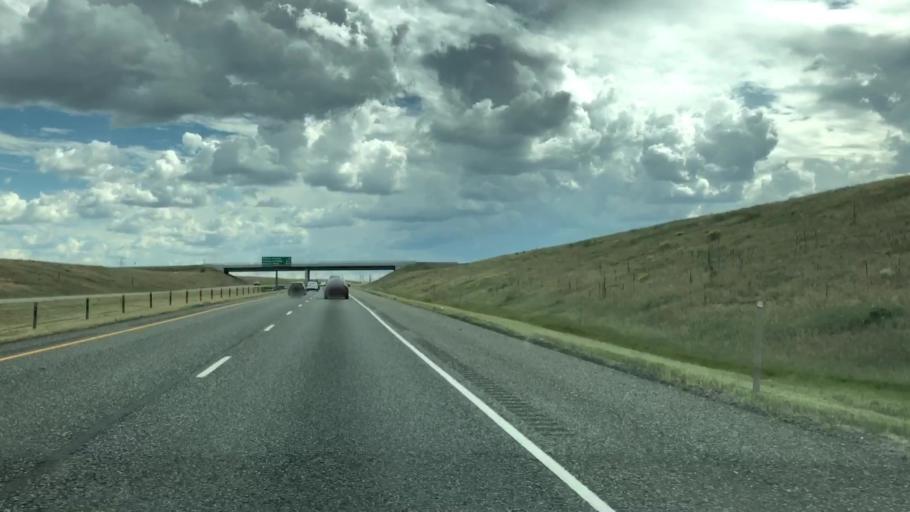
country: US
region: Colorado
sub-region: Adams County
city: Aurora
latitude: 39.6566
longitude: -104.7208
